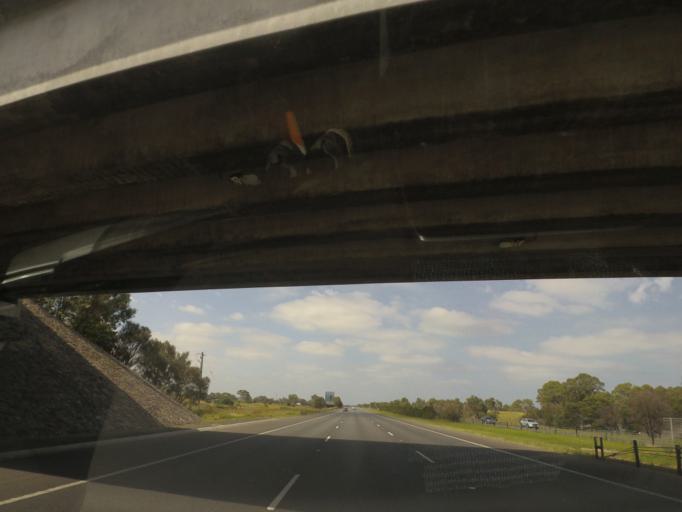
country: AU
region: Victoria
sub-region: Greater Dandenong
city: Keysborough
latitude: -38.0361
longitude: 145.1891
